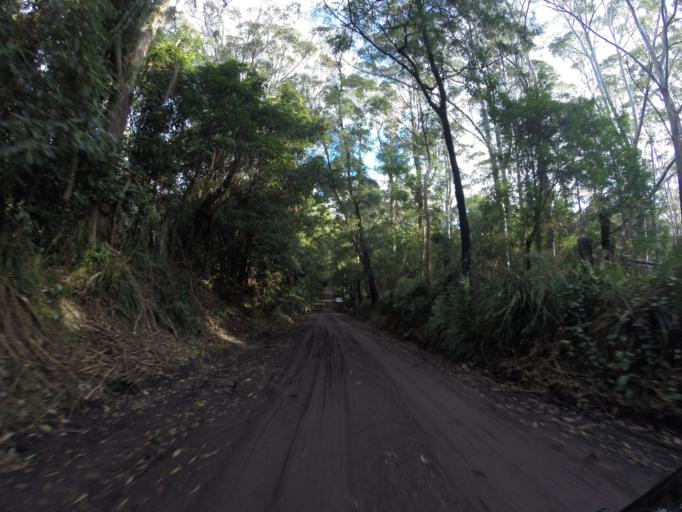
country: AU
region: New South Wales
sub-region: Wollongong
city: Cordeaux Heights
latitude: -34.4231
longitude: 150.7824
